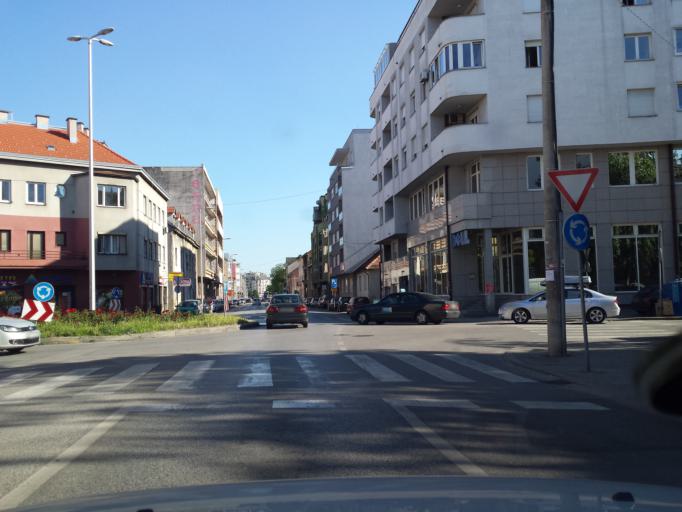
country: HR
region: Grad Zagreb
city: Zagreb - Centar
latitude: 45.8042
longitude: 15.9548
